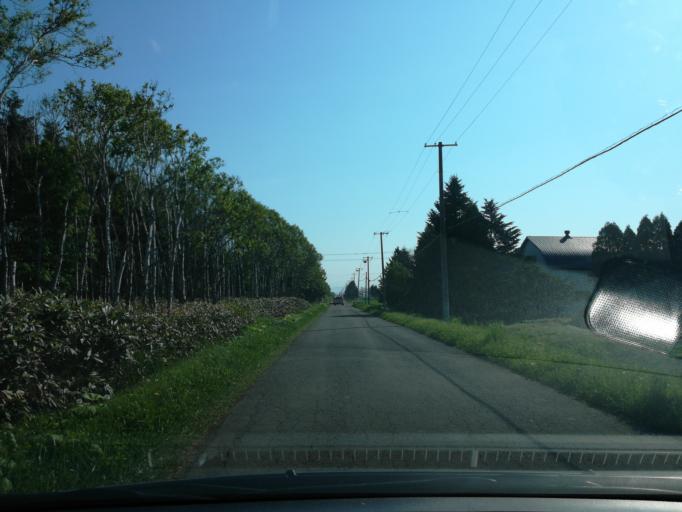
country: JP
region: Hokkaido
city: Ebetsu
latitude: 43.1215
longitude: 141.6576
